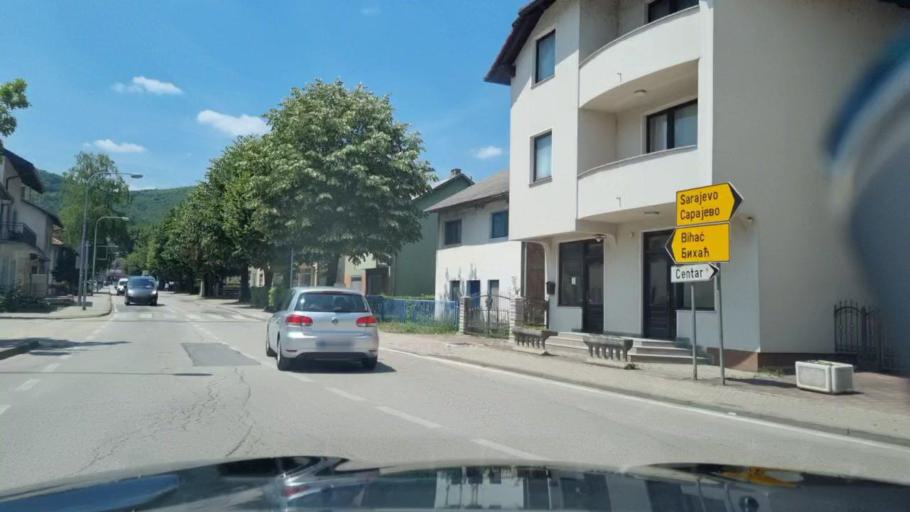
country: BA
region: Federation of Bosnia and Herzegovina
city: Kljuc
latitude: 44.5335
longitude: 16.7727
